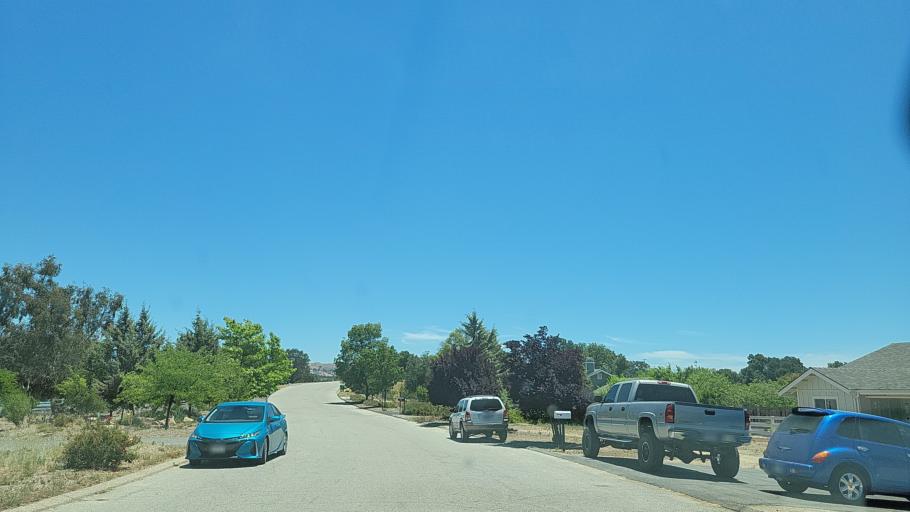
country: US
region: California
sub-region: San Luis Obispo County
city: Atascadero
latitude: 35.5182
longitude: -120.6821
